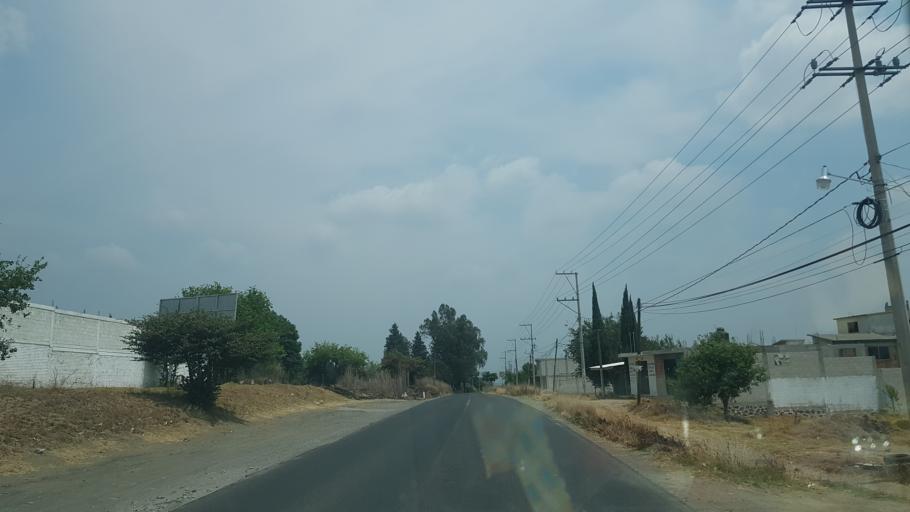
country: MX
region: Puebla
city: Huejotzingo
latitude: 19.1394
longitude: -98.4128
